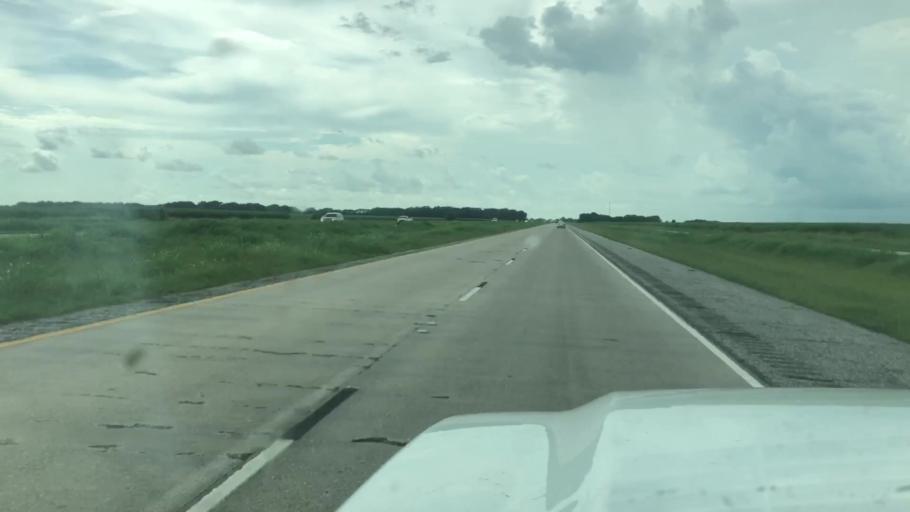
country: US
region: Louisiana
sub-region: Saint Mary Parish
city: Baldwin
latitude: 29.8506
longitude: -91.5968
